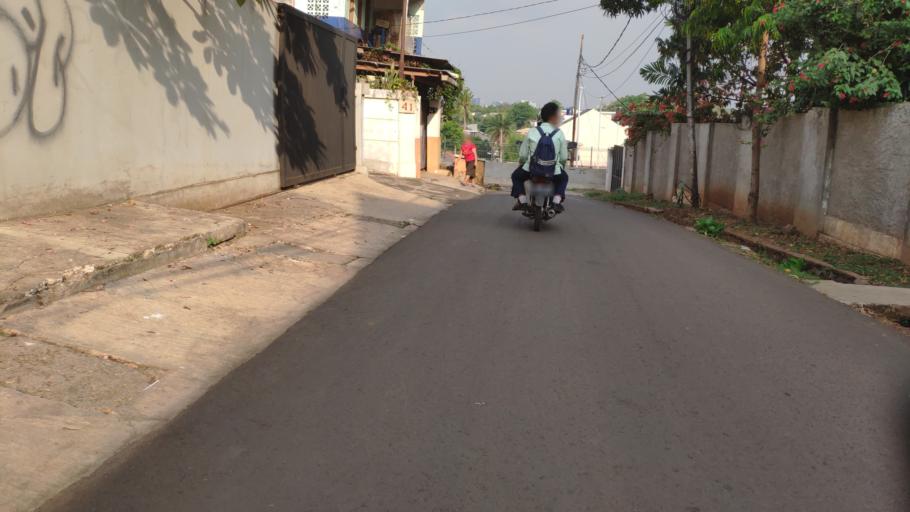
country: ID
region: West Java
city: Pamulang
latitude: -6.2973
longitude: 106.8038
